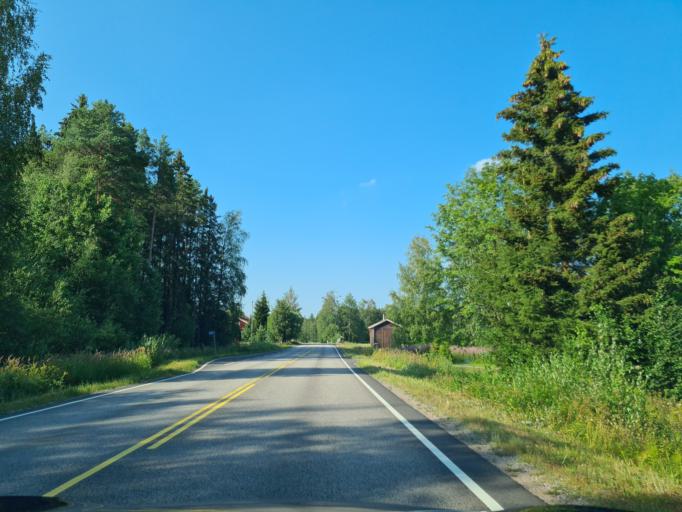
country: FI
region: Satakunta
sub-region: Pohjois-Satakunta
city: Karvia
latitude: 62.1984
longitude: 22.5963
